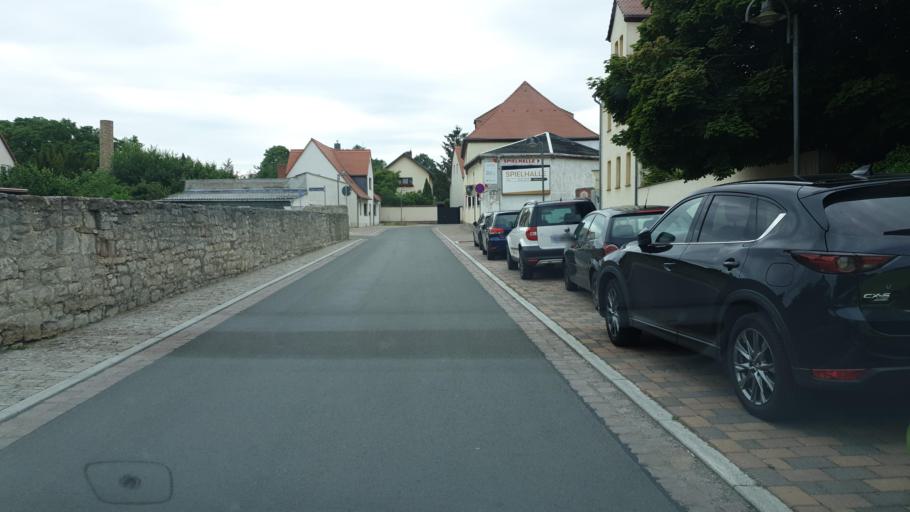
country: DE
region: Saxony-Anhalt
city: Querfurt
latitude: 51.3806
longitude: 11.6033
